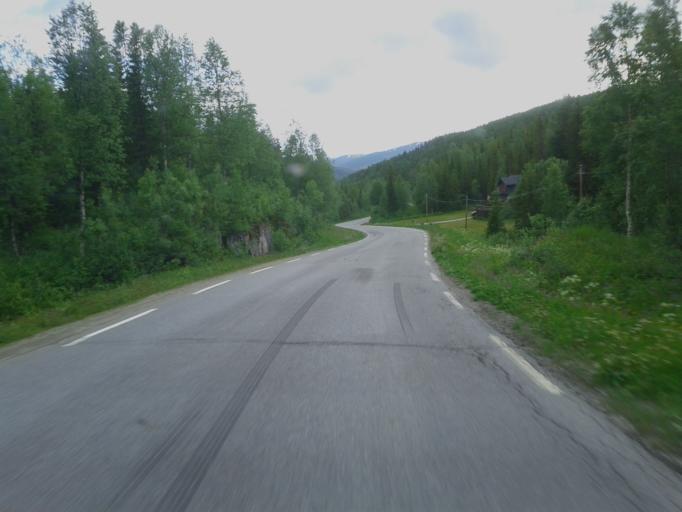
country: NO
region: Nordland
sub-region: Grane
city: Trofors
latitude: 65.5348
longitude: 13.6793
